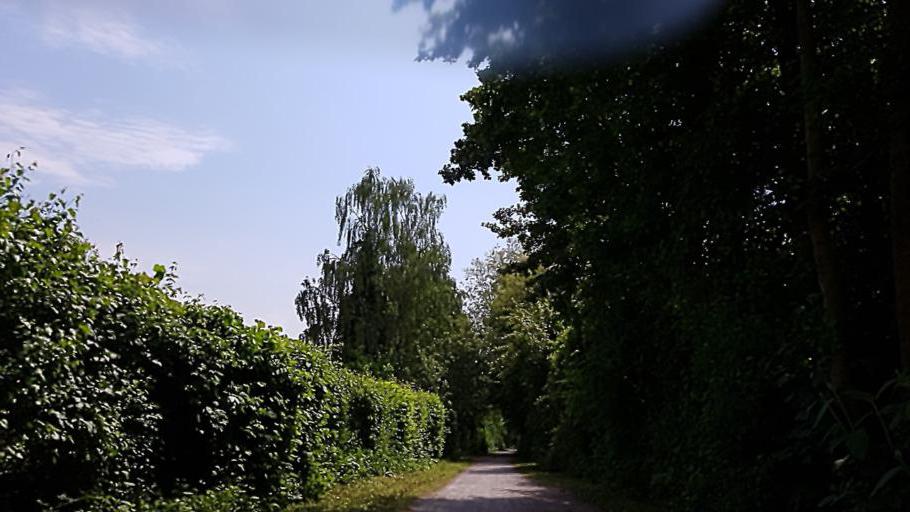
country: FR
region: Nord-Pas-de-Calais
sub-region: Departement du Nord
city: Conde-sur-l'Escaut
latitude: 50.4460
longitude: 3.5855
